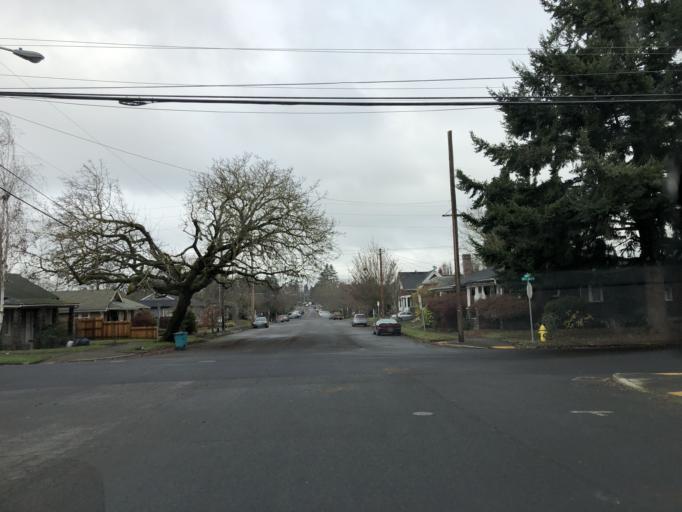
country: US
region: Washington
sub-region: Clark County
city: Vancouver
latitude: 45.6332
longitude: -122.6749
